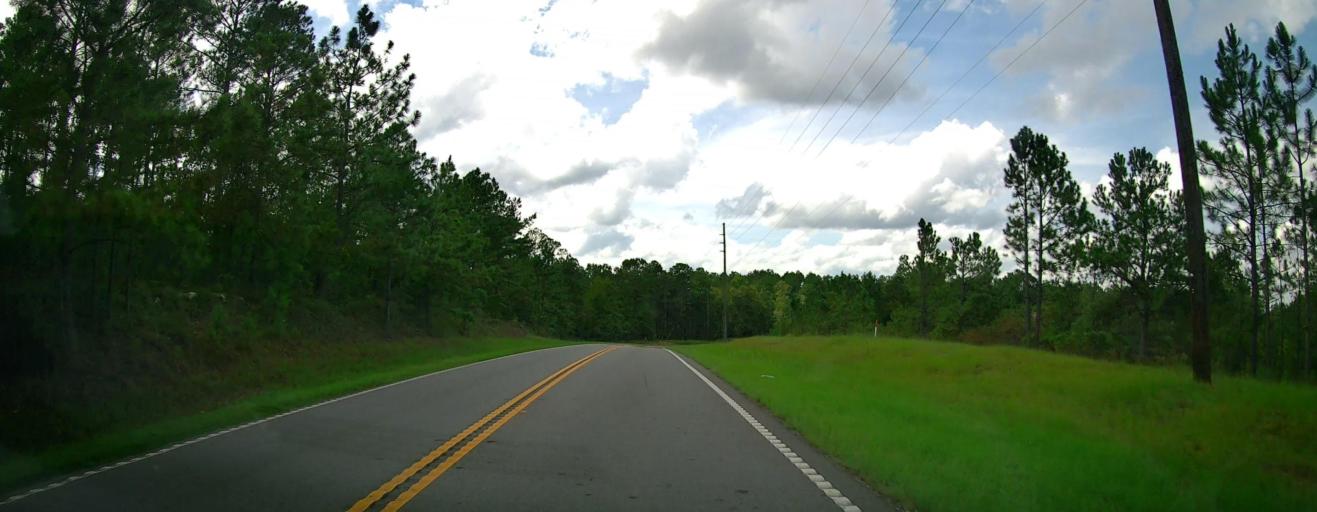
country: US
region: Georgia
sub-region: Talbot County
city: Talbotton
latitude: 32.6110
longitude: -84.4821
